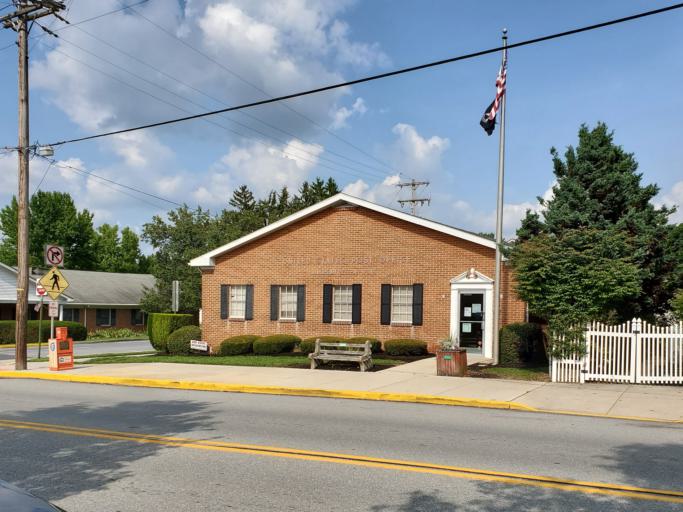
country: US
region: Pennsylvania
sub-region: York County
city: Dillsburg
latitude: 40.1118
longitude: -77.0359
